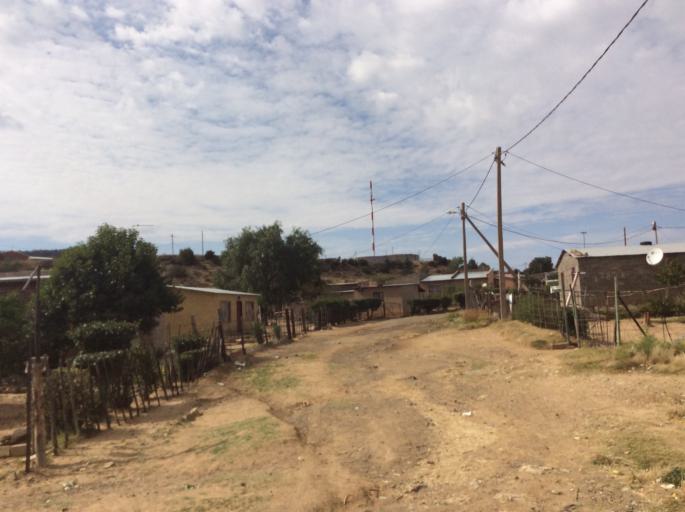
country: LS
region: Mafeteng
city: Mafeteng
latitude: -29.7230
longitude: 27.0273
